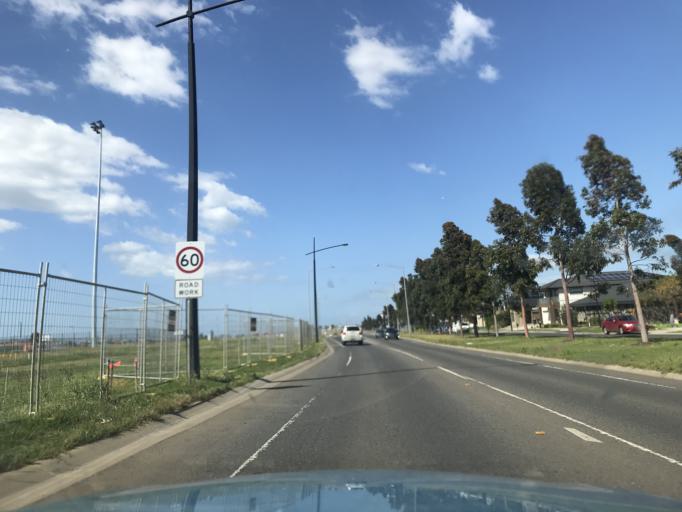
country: AU
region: Victoria
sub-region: Wyndham
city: Williams Landing
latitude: -37.8602
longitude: 144.7480
